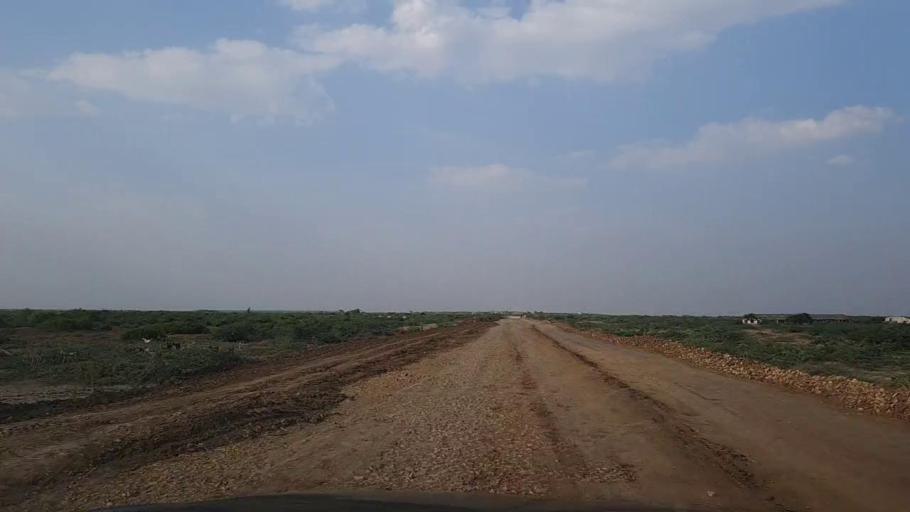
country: PK
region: Sindh
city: Gharo
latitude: 24.7897
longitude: 67.7445
